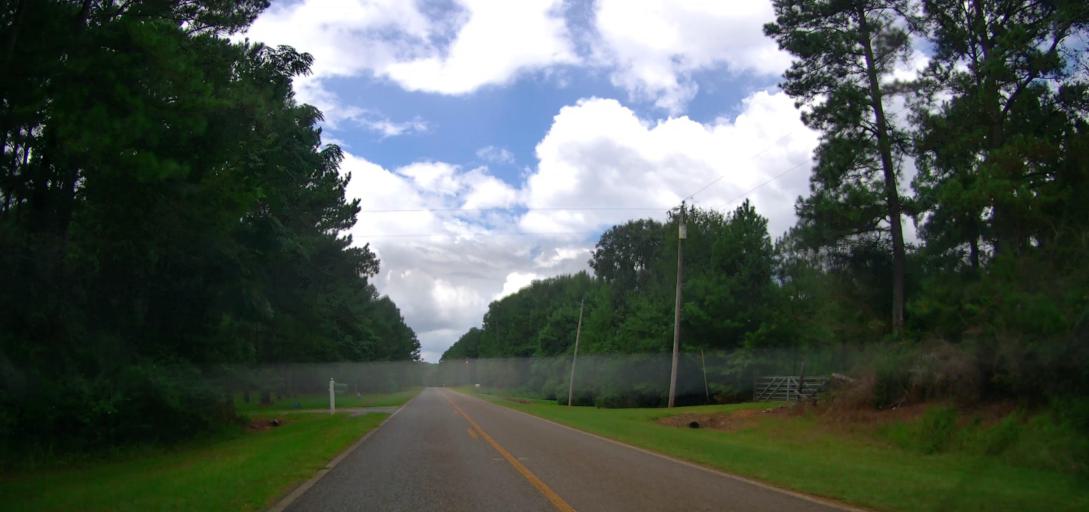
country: US
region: Georgia
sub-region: Pulaski County
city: Hawkinsville
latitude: 32.3452
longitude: -83.5613
